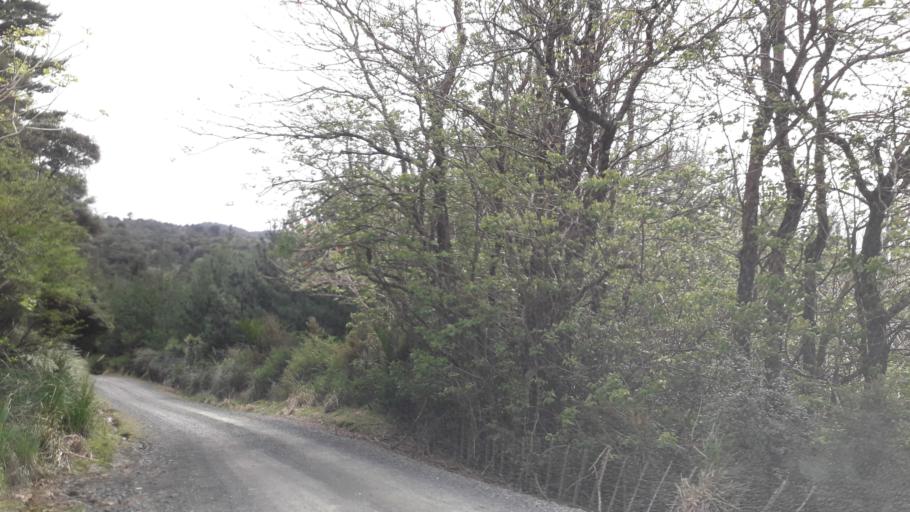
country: NZ
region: Northland
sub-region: Far North District
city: Kaitaia
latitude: -35.1959
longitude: 173.2854
